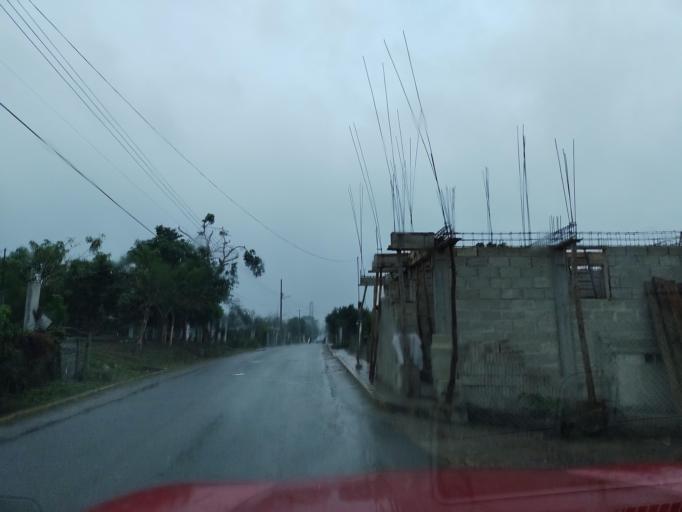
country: MX
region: Veracruz
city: Agua Dulce
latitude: 20.3374
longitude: -97.3138
